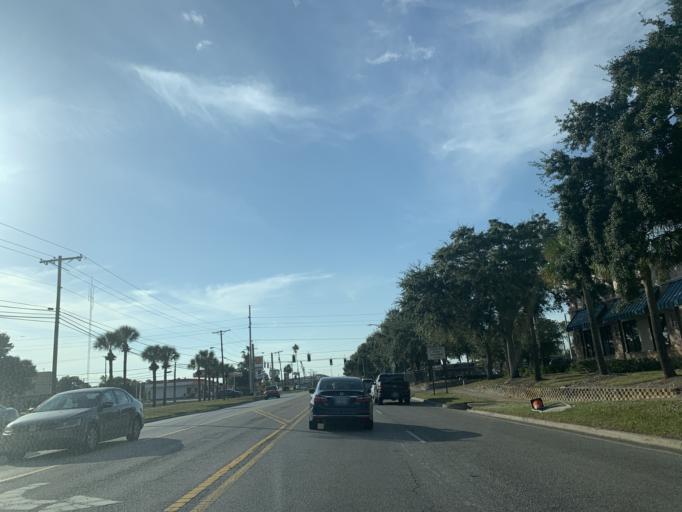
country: US
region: Florida
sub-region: Hillsborough County
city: Tampa
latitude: 27.8937
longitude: -82.5010
